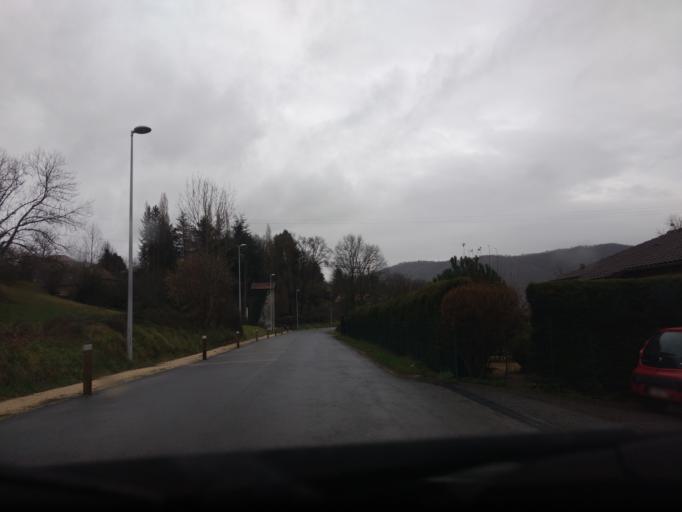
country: FR
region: Midi-Pyrenees
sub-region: Departement de l'Aveyron
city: Livinhac-le-Haut
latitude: 44.5988
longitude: 2.2318
